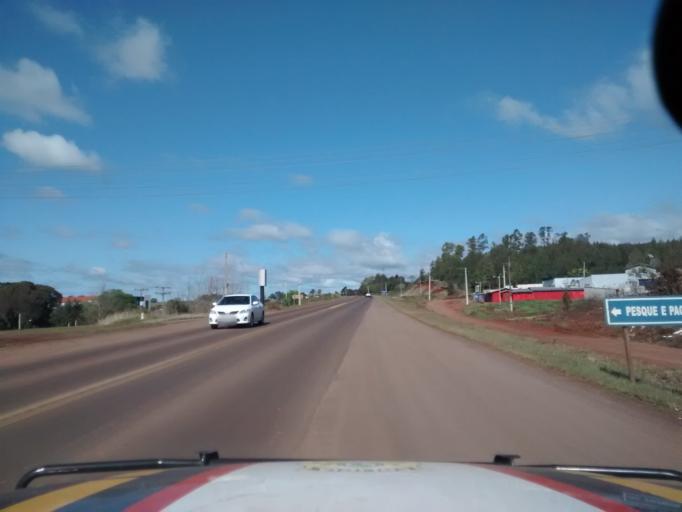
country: BR
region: Rio Grande do Sul
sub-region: Lagoa Vermelha
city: Lagoa Vermelha
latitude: -28.2159
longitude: -51.5101
